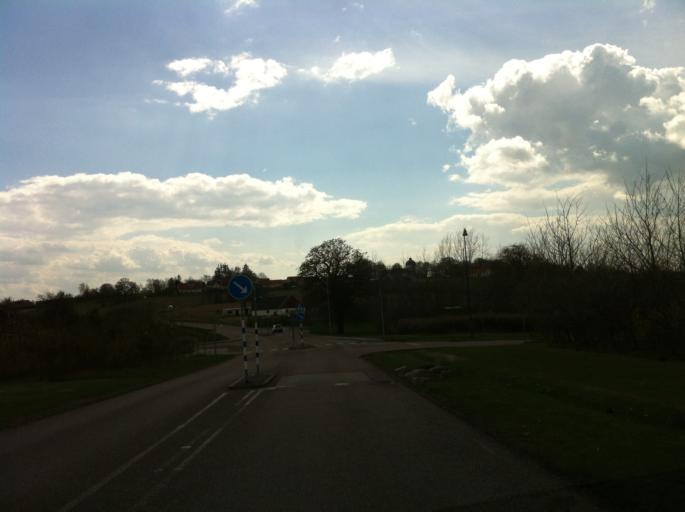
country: SE
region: Skane
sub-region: Eslovs Kommun
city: Eslov
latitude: 55.8348
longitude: 13.2838
